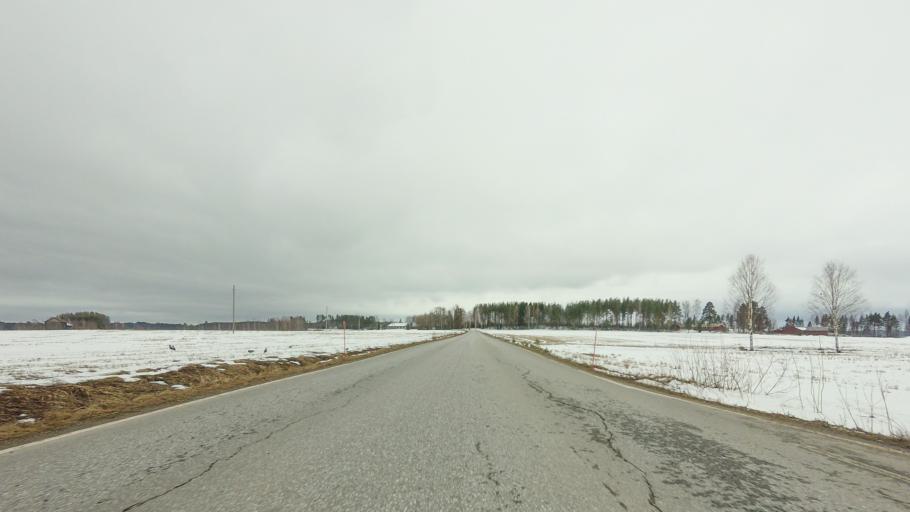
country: FI
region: Southern Savonia
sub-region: Savonlinna
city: Savonlinna
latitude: 61.9625
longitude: 28.8291
